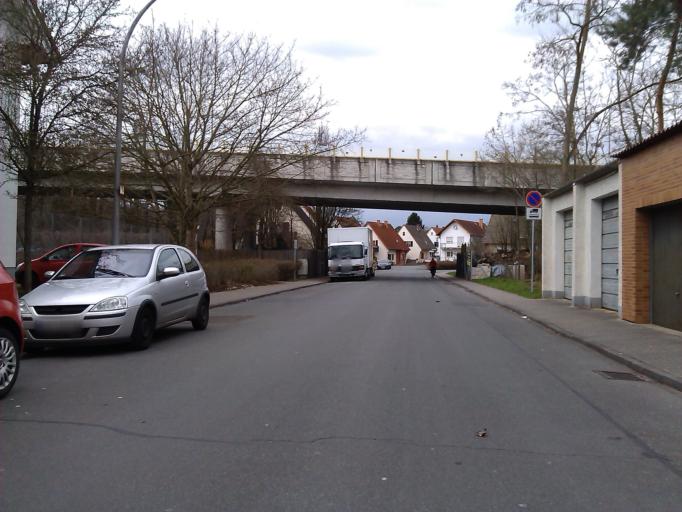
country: DE
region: Hesse
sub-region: Regierungsbezirk Darmstadt
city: Nauheim
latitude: 49.9463
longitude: 8.4441
